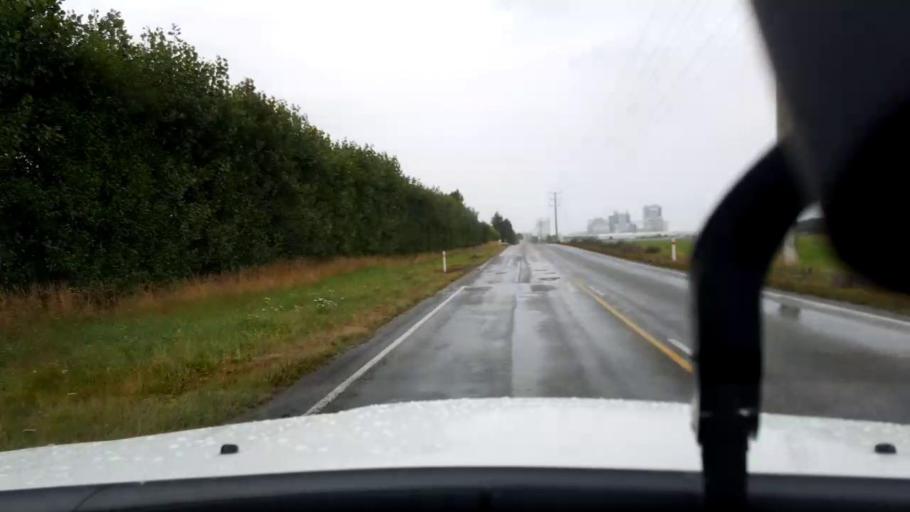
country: NZ
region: Canterbury
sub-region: Timaru District
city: Timaru
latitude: -44.2035
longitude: 171.3726
